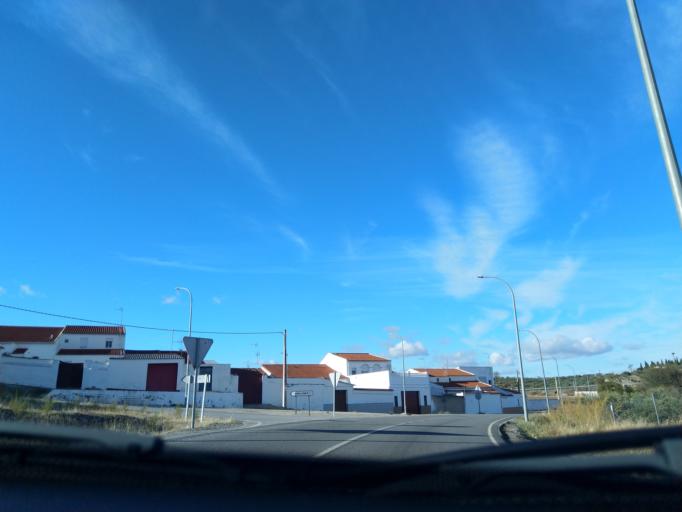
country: ES
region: Extremadura
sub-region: Provincia de Badajoz
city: Ahillones
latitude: 38.2614
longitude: -5.8620
